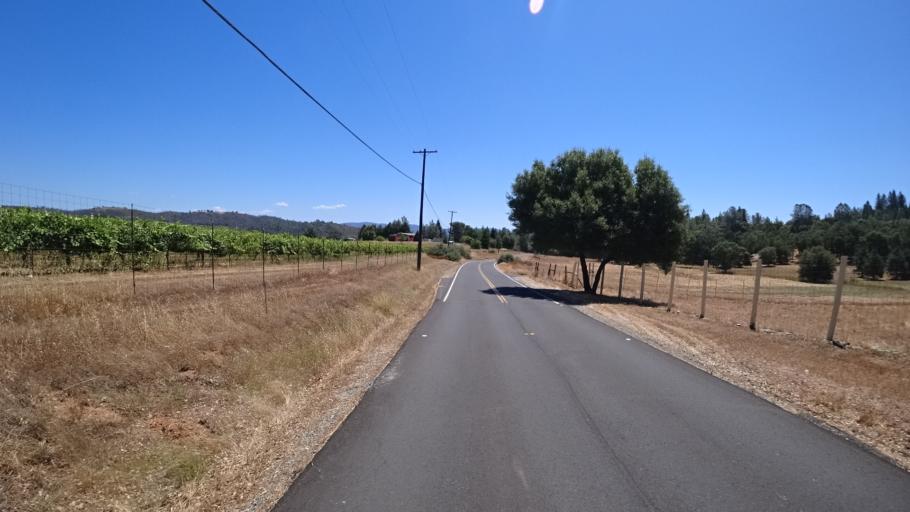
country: US
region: California
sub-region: Calaveras County
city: Mountain Ranch
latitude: 38.2158
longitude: -120.5414
